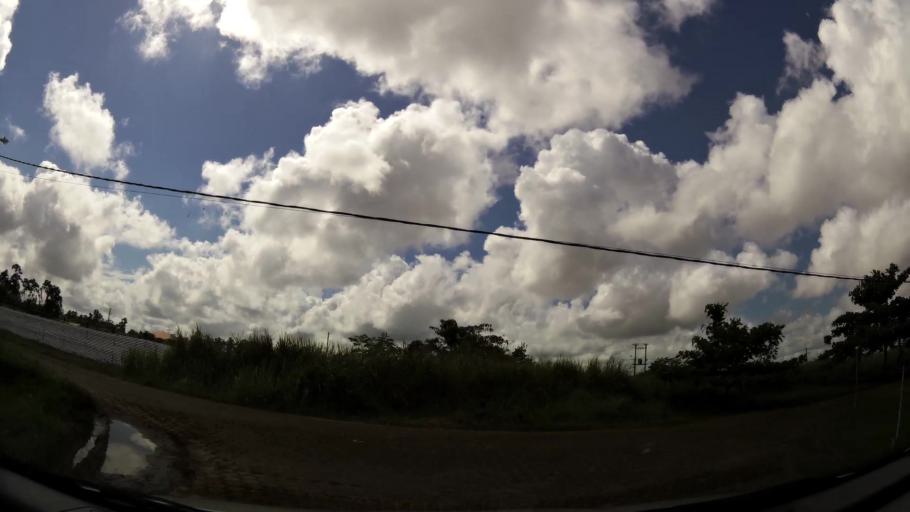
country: SR
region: Commewijne
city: Nieuw Amsterdam
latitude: 5.8688
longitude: -55.1215
